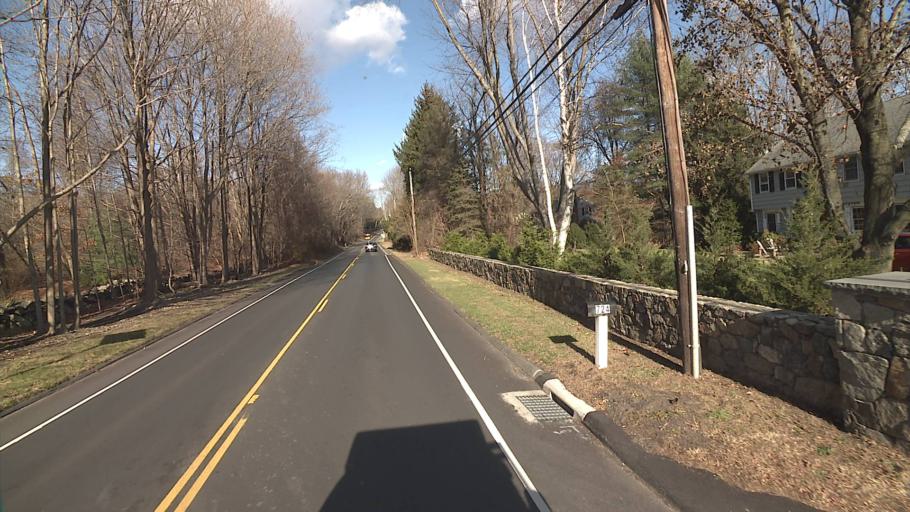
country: US
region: Connecticut
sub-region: Fairfield County
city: Bethel
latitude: 41.3343
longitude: -73.4182
